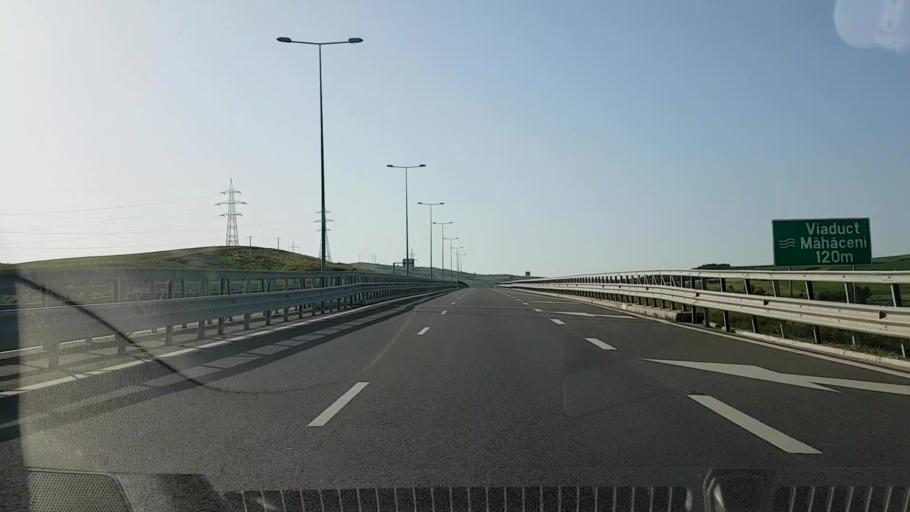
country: RO
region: Alba
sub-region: Comuna Unirea
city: Unirea
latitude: 46.4553
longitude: 23.7892
